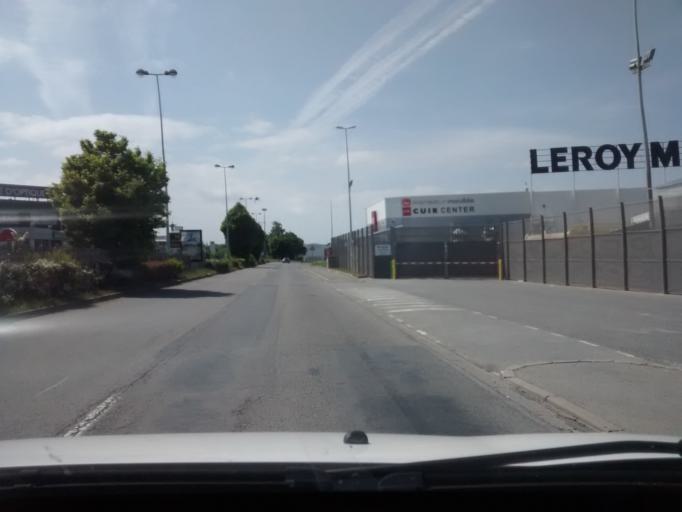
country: FR
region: Brittany
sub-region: Departement des Cotes-d'Armor
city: Langueux
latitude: 48.4967
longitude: -2.7295
